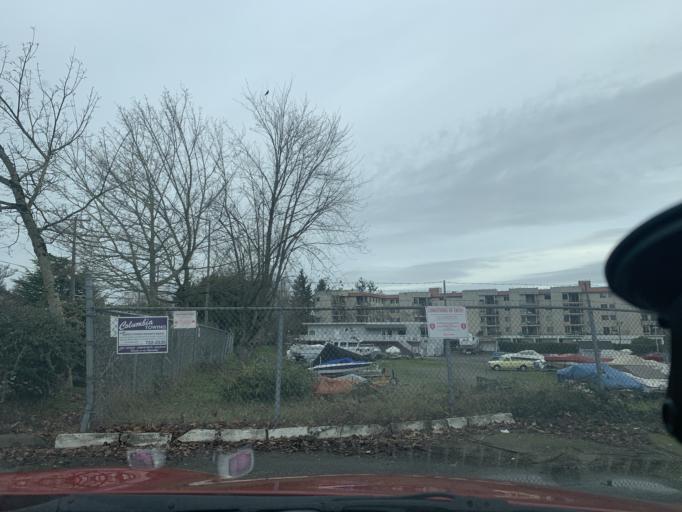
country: US
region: Washington
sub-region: King County
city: Bryn Mawr-Skyway
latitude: 47.5208
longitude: -122.2631
